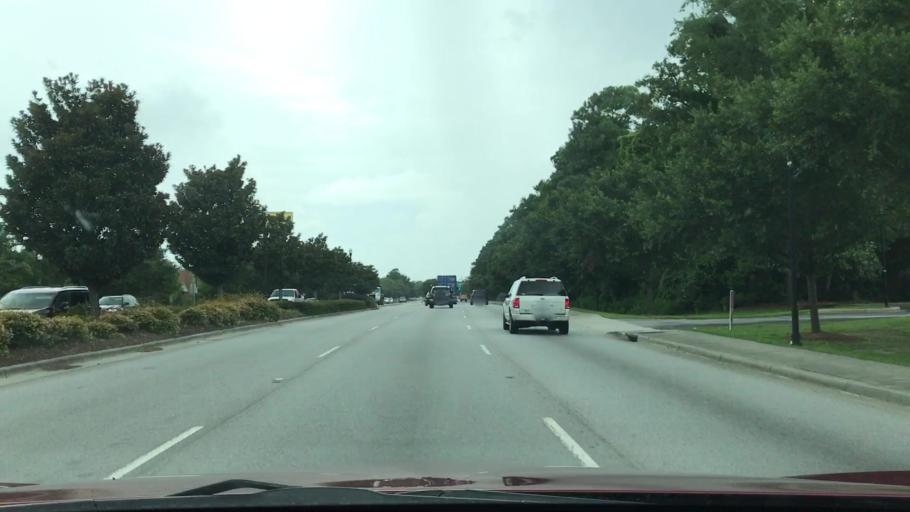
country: US
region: South Carolina
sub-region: Charleston County
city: Mount Pleasant
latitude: 32.8329
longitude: -79.8273
